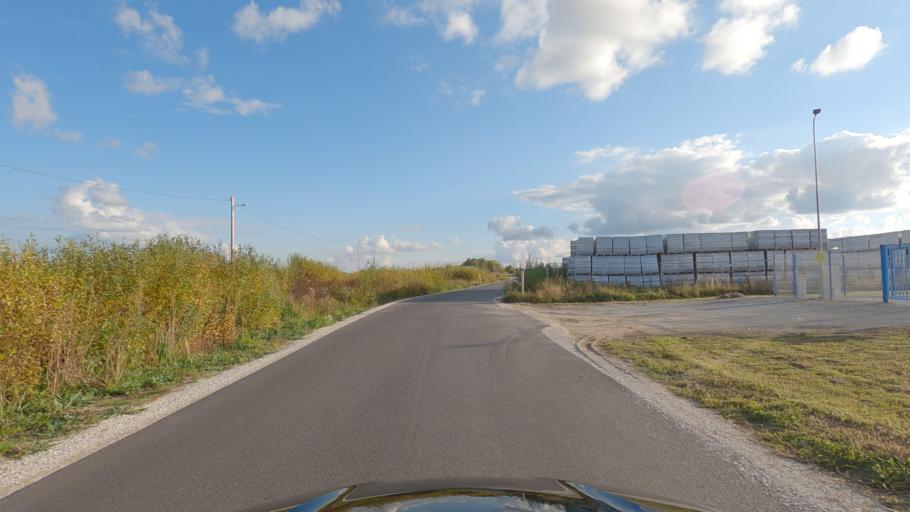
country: EE
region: Harju
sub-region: Saku vald
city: Saku
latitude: 59.2904
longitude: 24.6660
